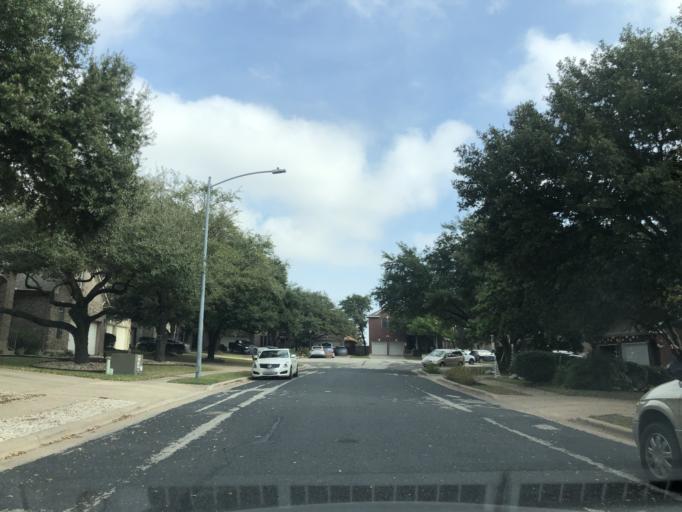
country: US
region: Texas
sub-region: Travis County
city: Wells Branch
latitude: 30.4222
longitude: -97.6819
